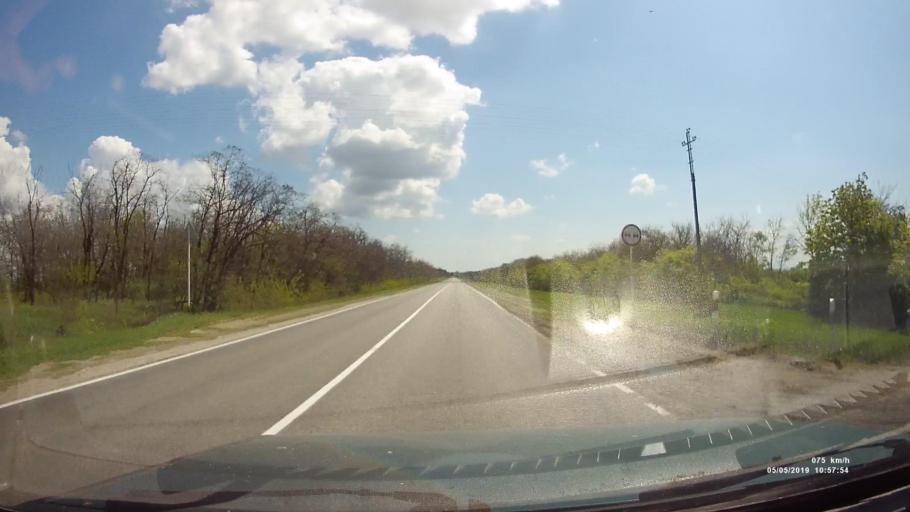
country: RU
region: Rostov
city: Ust'-Donetskiy
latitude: 47.6713
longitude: 40.8439
